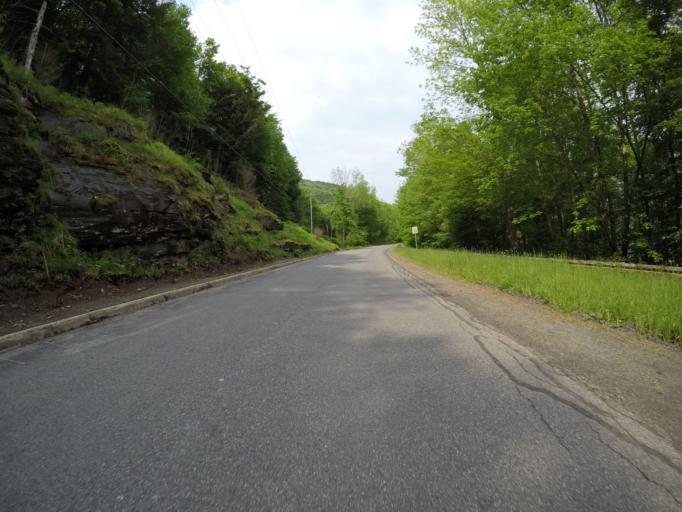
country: US
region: New York
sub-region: Sullivan County
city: Livingston Manor
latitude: 42.0821
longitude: -74.7892
